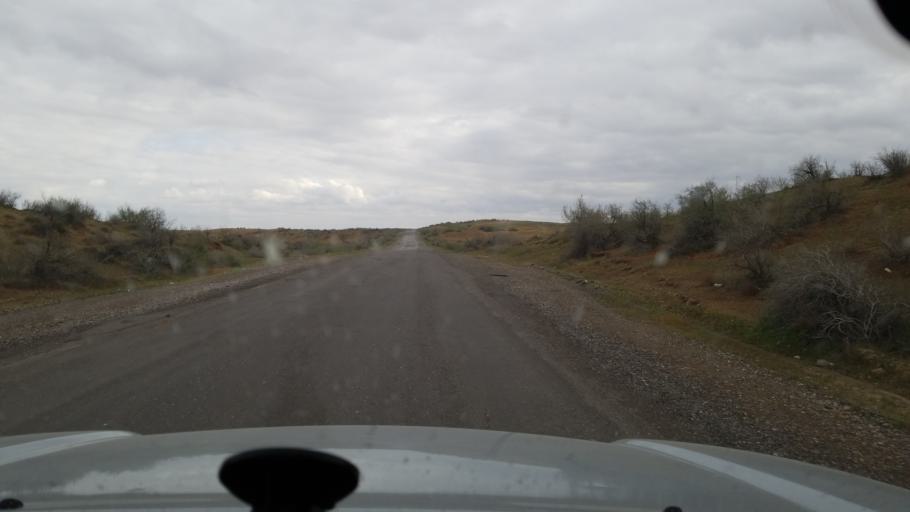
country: TM
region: Mary
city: Serhetabat
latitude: 36.0862
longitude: 62.6132
